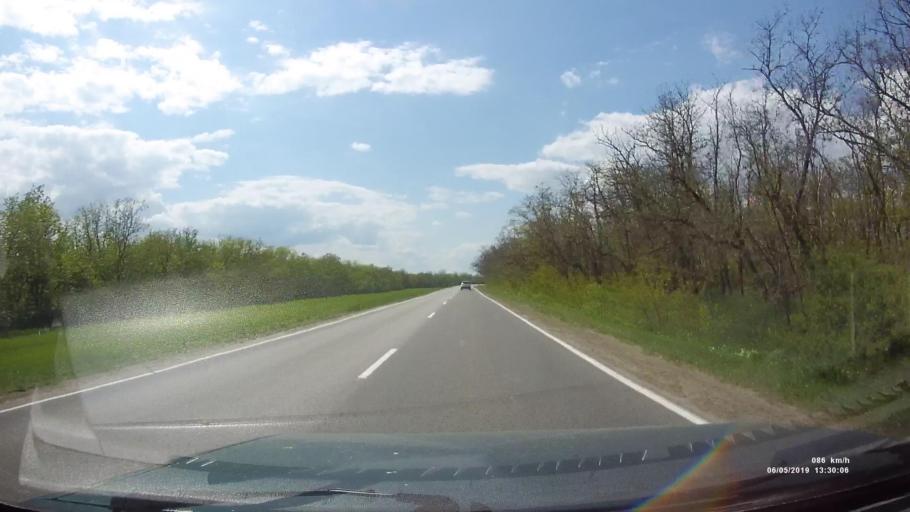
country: RU
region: Rostov
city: Ust'-Donetskiy
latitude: 47.6711
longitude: 40.8327
